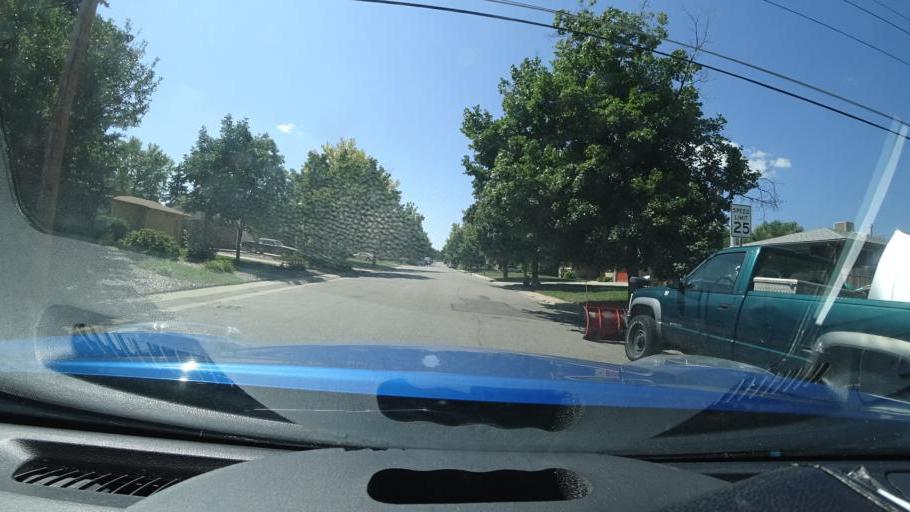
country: US
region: Colorado
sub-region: Adams County
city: Aurora
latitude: 39.7229
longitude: -104.8745
